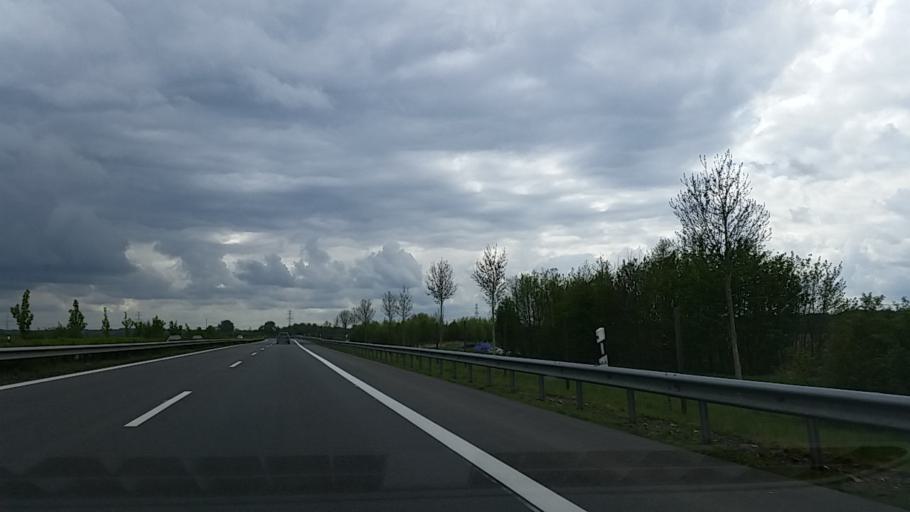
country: DE
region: Lower Saxony
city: Horneburg
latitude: 53.5321
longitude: 9.5788
